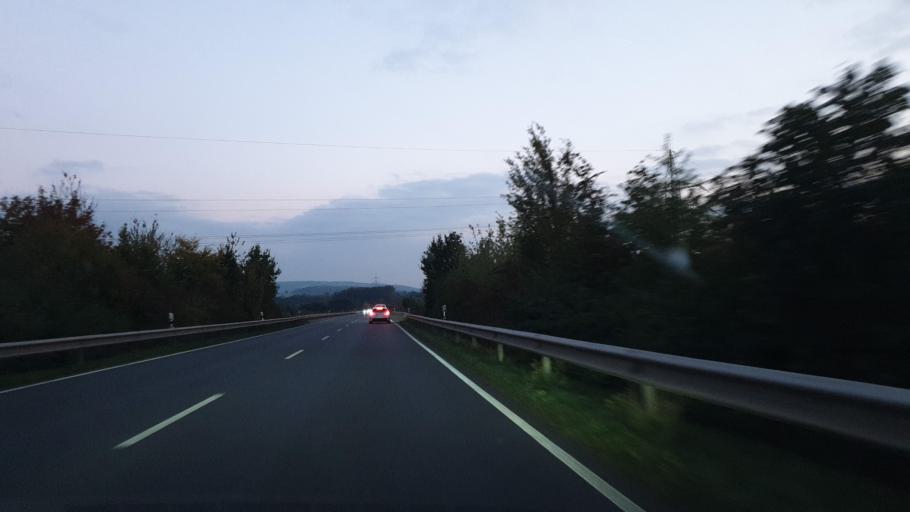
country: DE
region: North Rhine-Westphalia
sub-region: Regierungsbezirk Detmold
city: Kirchlengern
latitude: 52.1976
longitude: 8.6573
